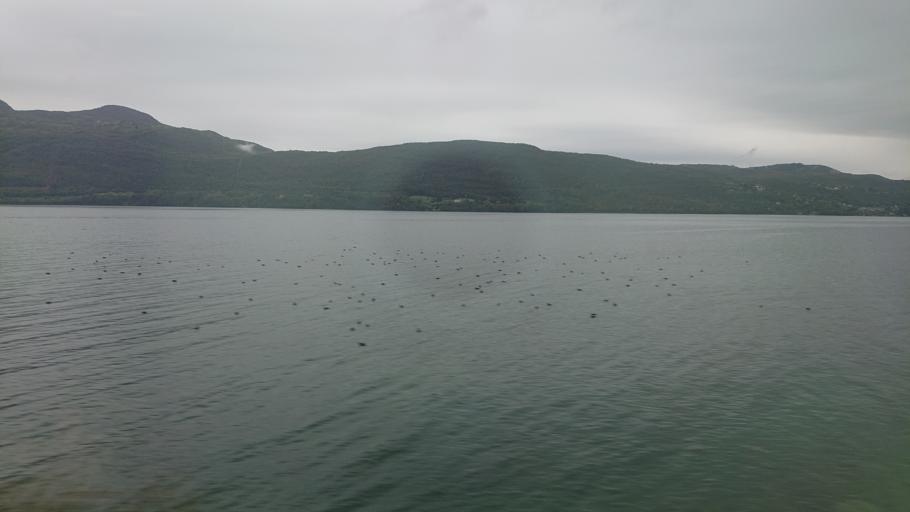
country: FR
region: Rhone-Alpes
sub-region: Departement de la Savoie
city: Chatillon
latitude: 45.7811
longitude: 5.8641
